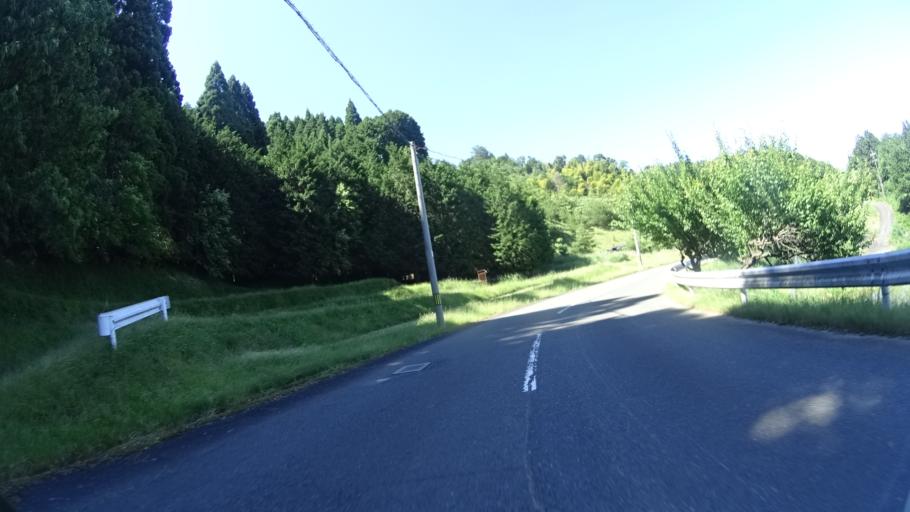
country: JP
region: Kyoto
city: Fukuchiyama
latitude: 35.3790
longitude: 135.0606
